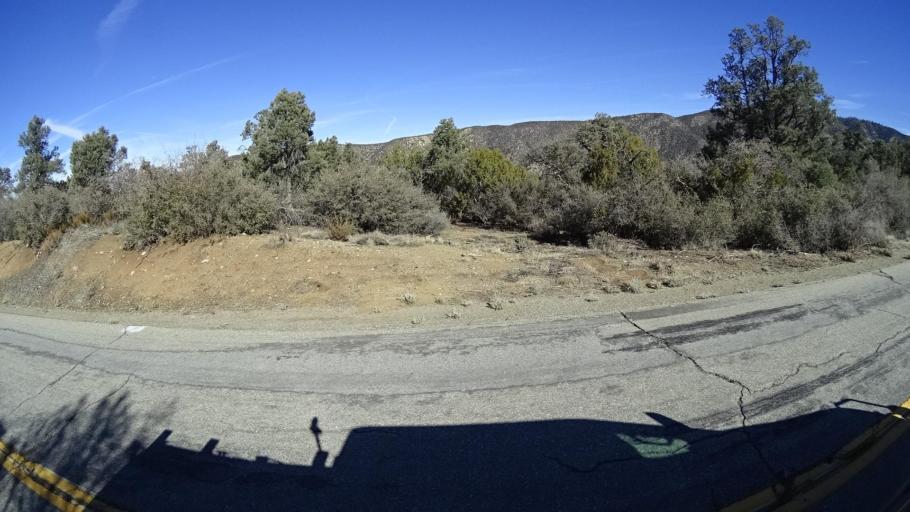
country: US
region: California
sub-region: Kern County
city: Pine Mountain Club
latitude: 34.8710
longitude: -119.2667
